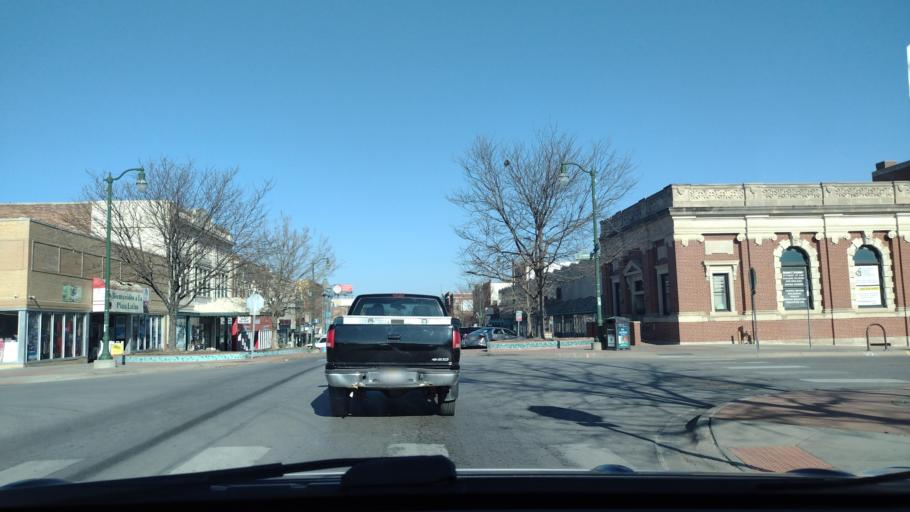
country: US
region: Nebraska
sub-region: Douglas County
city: Omaha
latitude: 41.2081
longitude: -95.9470
